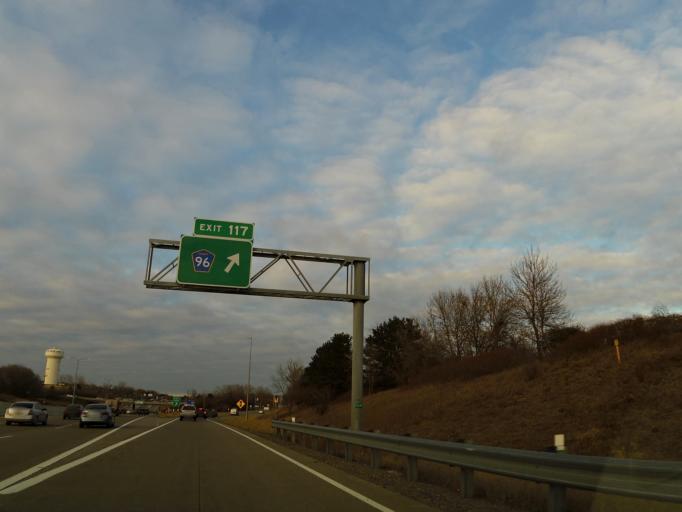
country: US
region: Minnesota
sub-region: Ramsey County
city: Vadnais Heights
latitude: 45.0758
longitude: -93.0524
